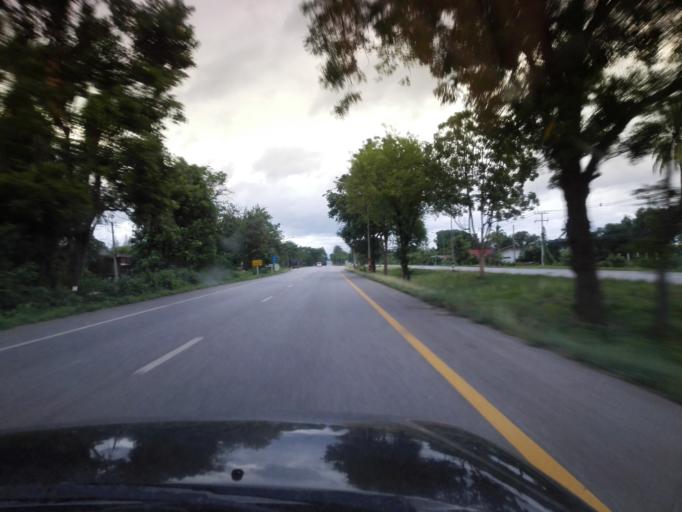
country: TH
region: Tak
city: Tak
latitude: 16.8025
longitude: 99.1472
